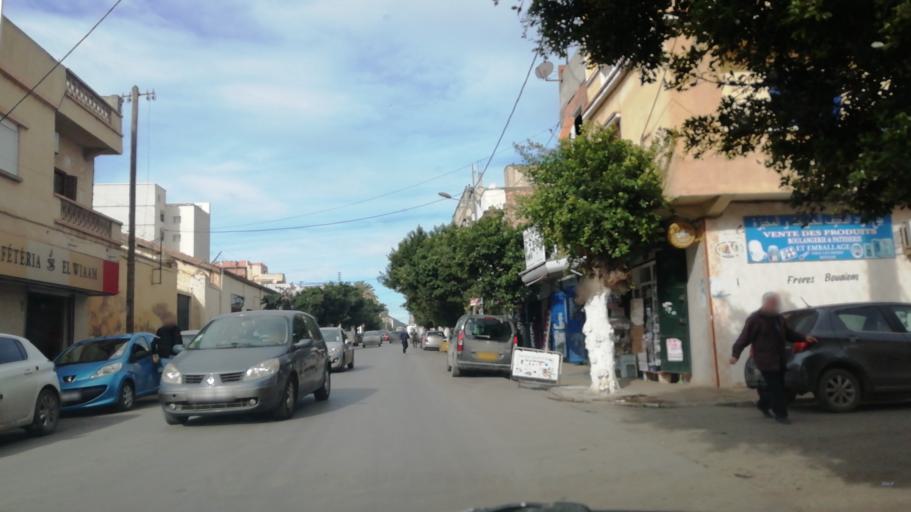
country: DZ
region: Oran
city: Oran
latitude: 35.6907
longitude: -0.6265
